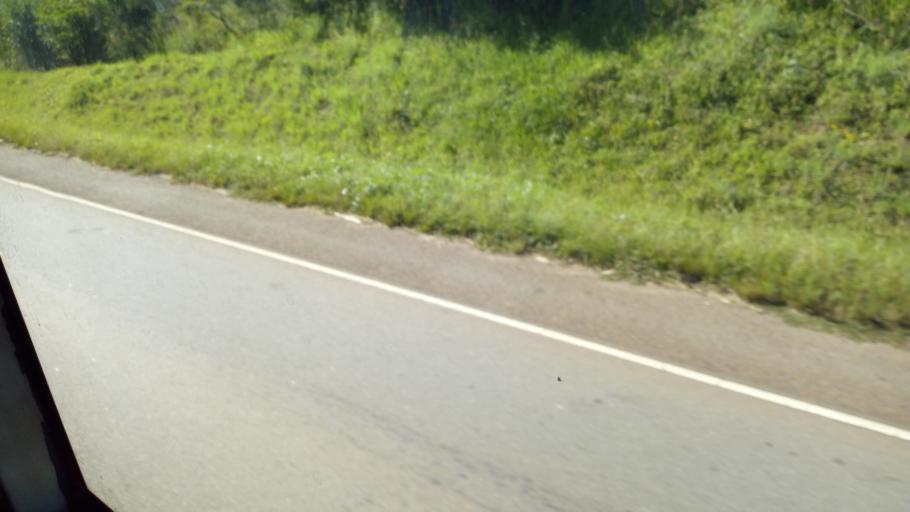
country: UG
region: Central Region
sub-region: Lyantonde District
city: Lyantonde
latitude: -0.4379
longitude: 31.0850
